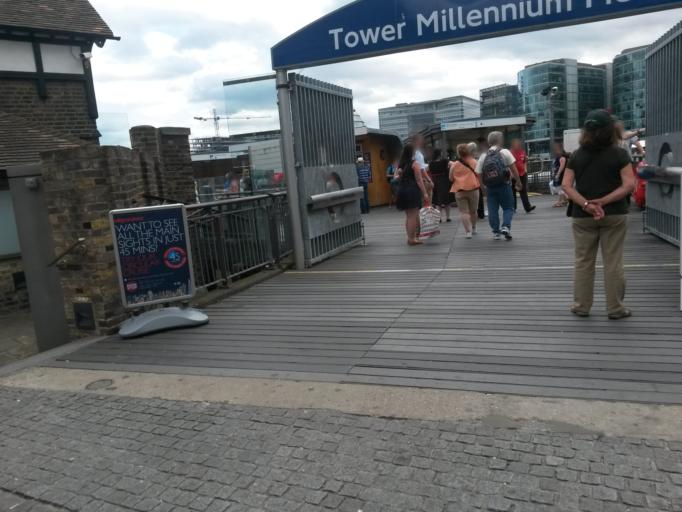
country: GB
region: England
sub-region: Greater London
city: City of London
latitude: 51.5081
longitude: -0.0793
